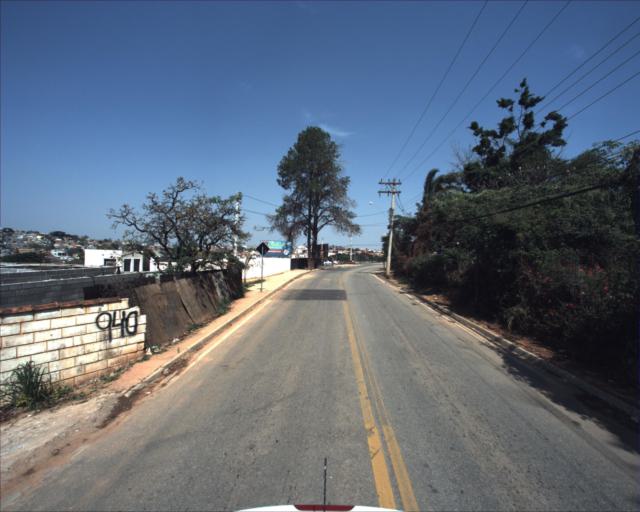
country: BR
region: Sao Paulo
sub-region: Sorocaba
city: Sorocaba
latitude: -23.4531
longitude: -47.4960
